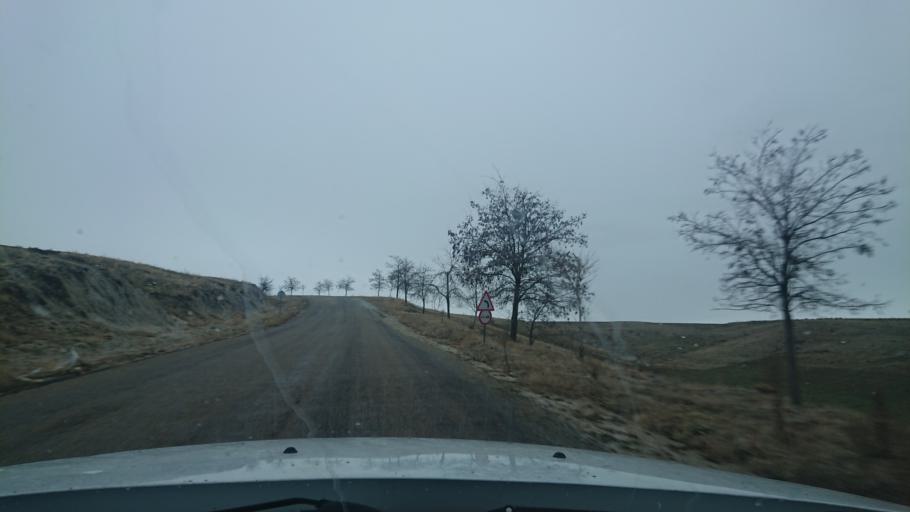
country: TR
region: Aksaray
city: Agacoren
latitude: 38.8578
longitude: 33.9522
